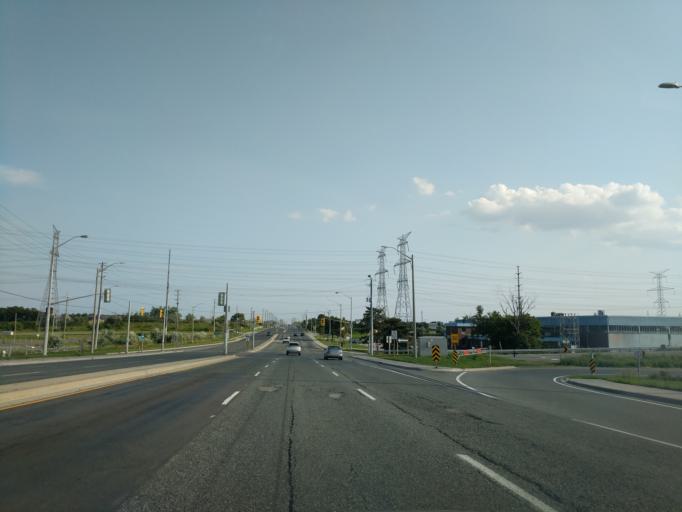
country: CA
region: Ontario
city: Willowdale
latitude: 43.8401
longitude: -79.3557
